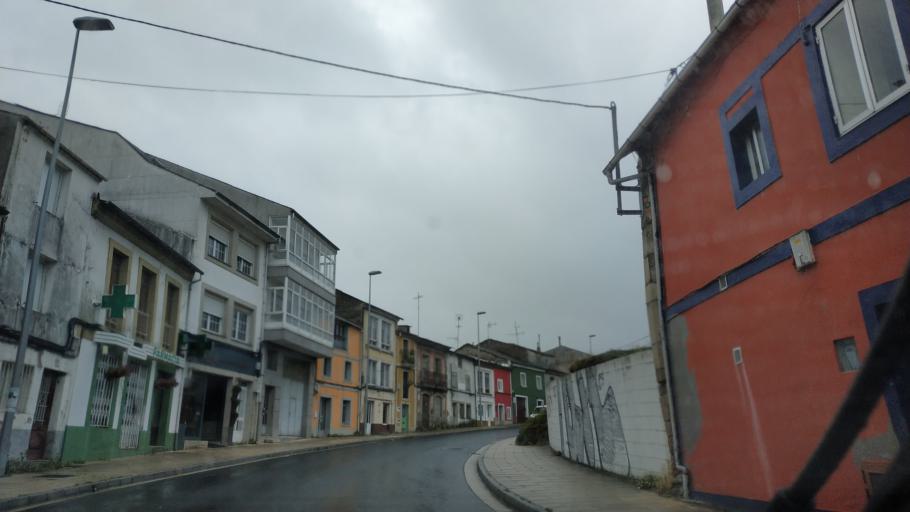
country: ES
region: Galicia
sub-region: Provincia de Lugo
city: Lugo
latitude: 43.0011
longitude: -7.5633
